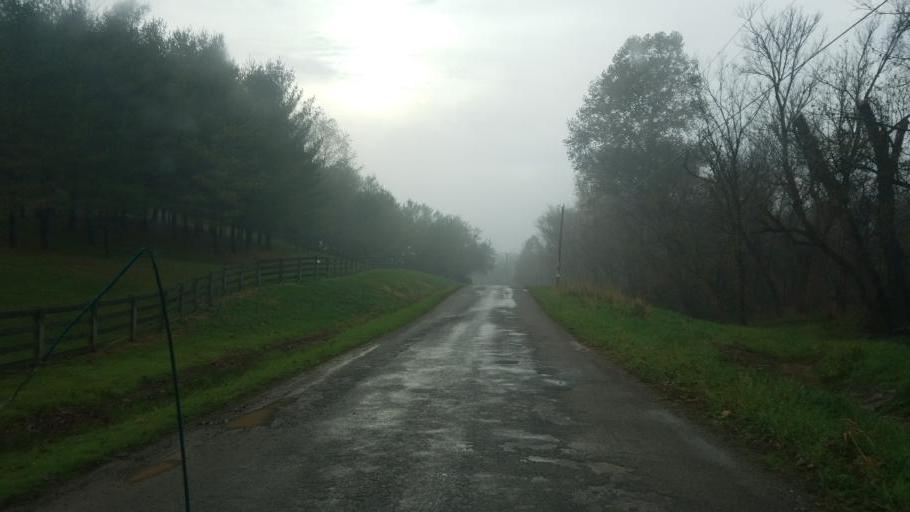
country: US
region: Ohio
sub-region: Athens County
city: Glouster
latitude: 39.4402
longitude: -81.9203
